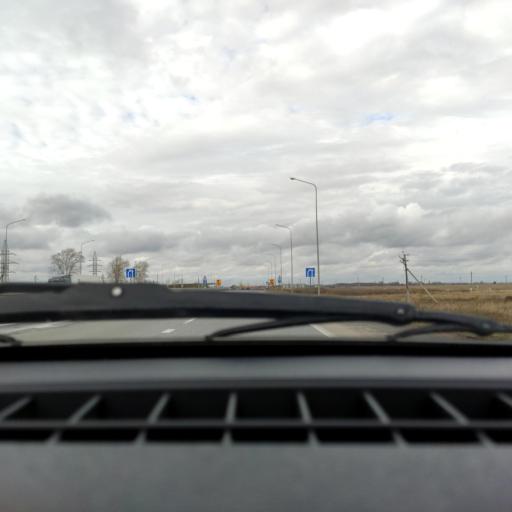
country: RU
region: Bashkortostan
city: Asanovo
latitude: 54.8981
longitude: 55.6355
